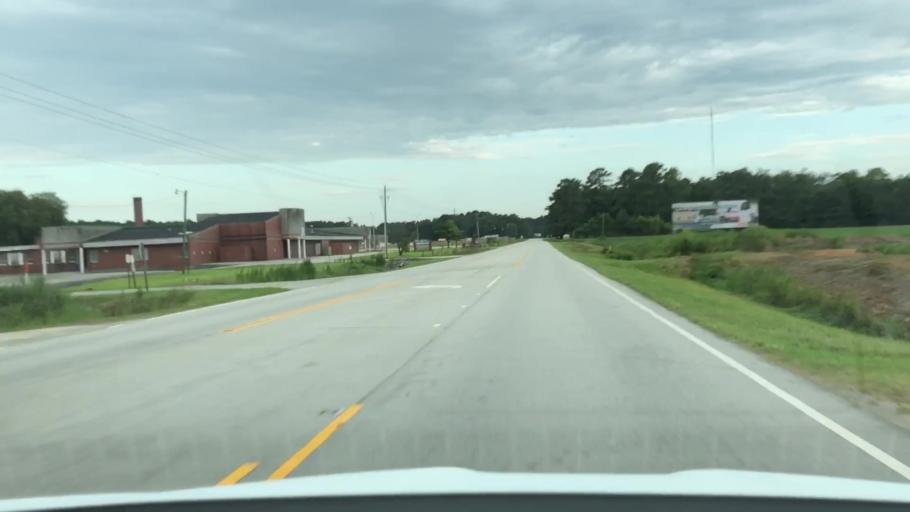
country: US
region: North Carolina
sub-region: Jones County
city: Trenton
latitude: 35.0347
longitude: -77.3316
